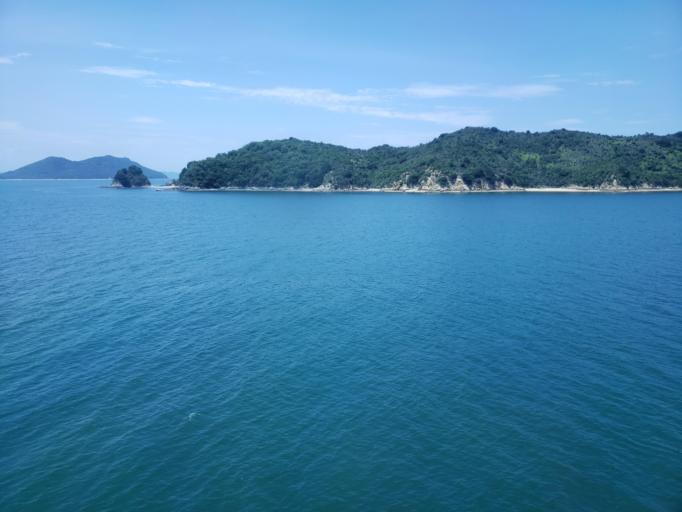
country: JP
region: Kagawa
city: Takamatsu-shi
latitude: 34.3962
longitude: 134.1052
